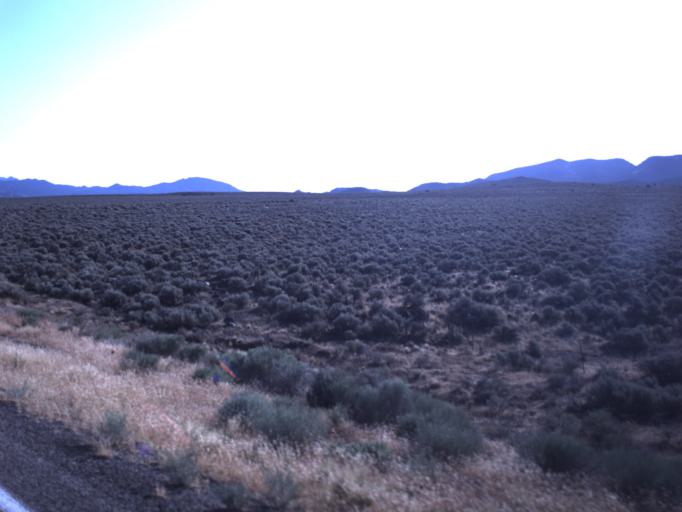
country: US
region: Utah
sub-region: Beaver County
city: Milford
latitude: 38.1563
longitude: -112.9578
